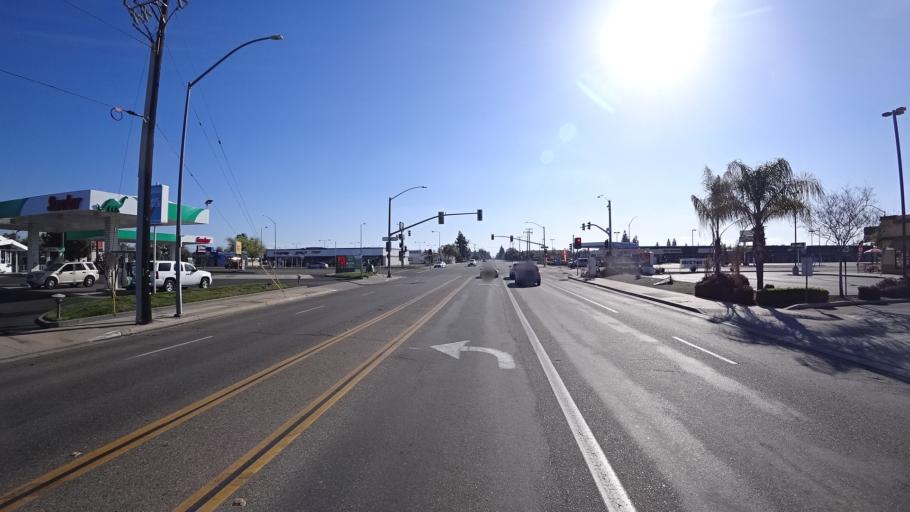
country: US
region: California
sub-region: Fresno County
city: Fresno
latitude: 36.8157
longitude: -119.7912
